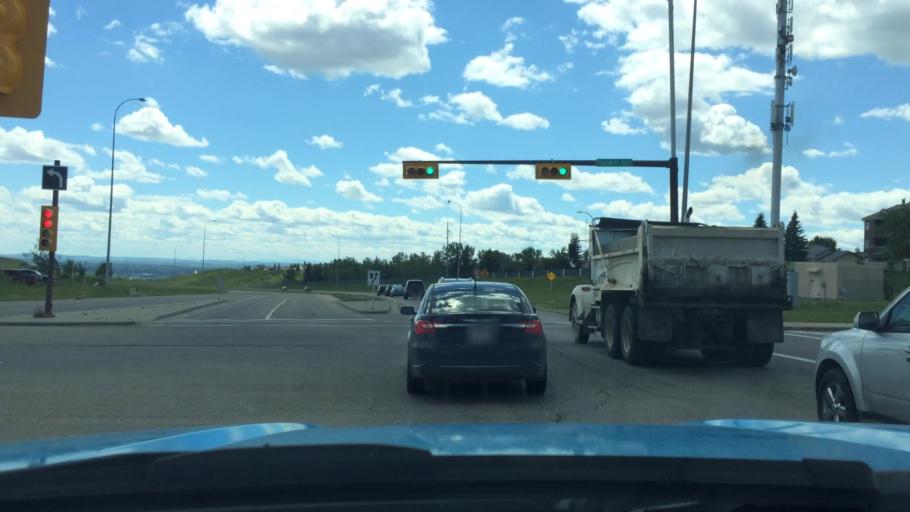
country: CA
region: Alberta
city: Calgary
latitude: 51.1270
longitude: -114.1332
